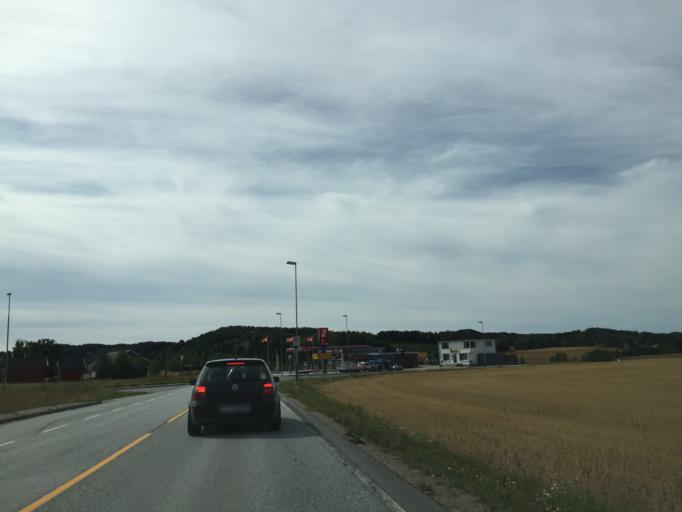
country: NO
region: Ostfold
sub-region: Fredrikstad
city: Fredrikstad
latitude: 59.2624
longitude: 10.8931
